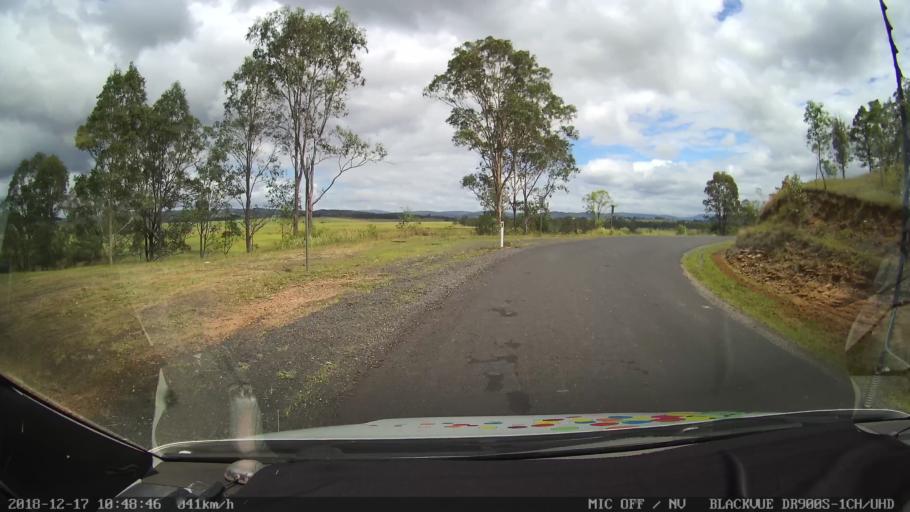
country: AU
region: New South Wales
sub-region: Clarence Valley
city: Gordon
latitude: -28.8705
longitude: 152.5715
